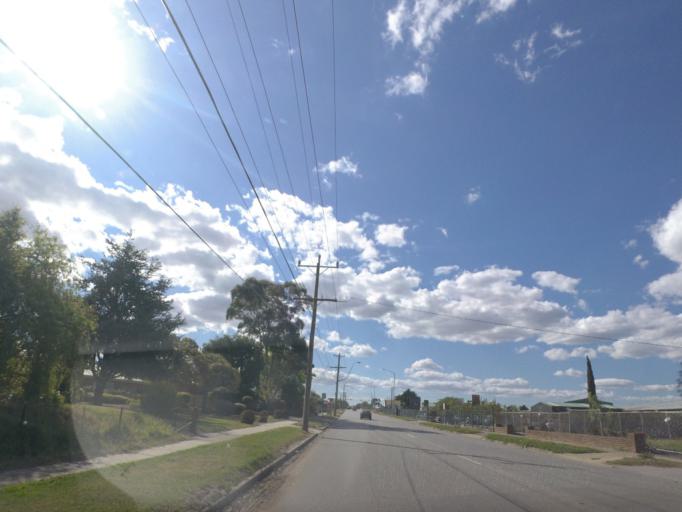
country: AU
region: Victoria
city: Heatherton
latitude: -37.9583
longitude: 145.1010
